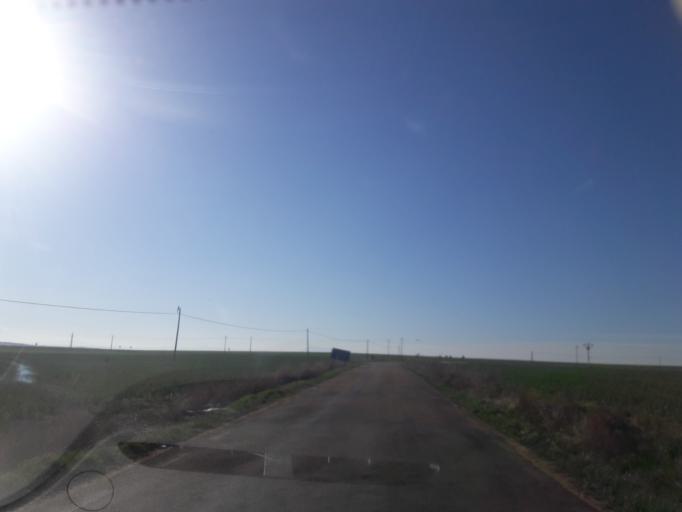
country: ES
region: Castille and Leon
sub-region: Provincia de Salamanca
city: Penarandilla
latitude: 40.8717
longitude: -5.3888
